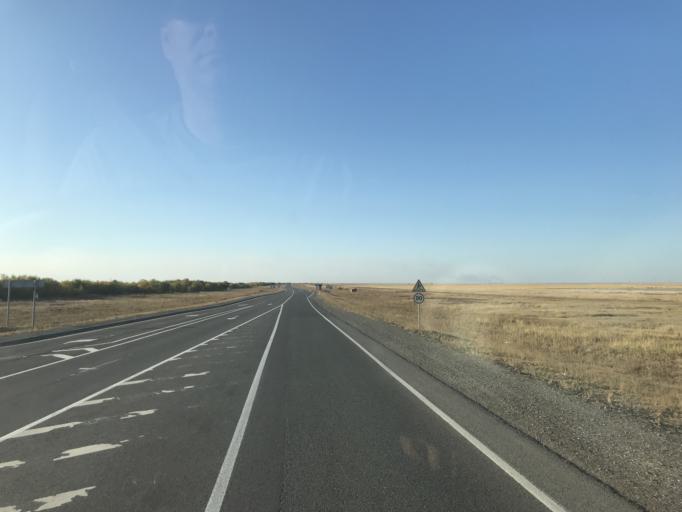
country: KZ
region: Pavlodar
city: Aksu
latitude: 52.0178
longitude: 77.2335
